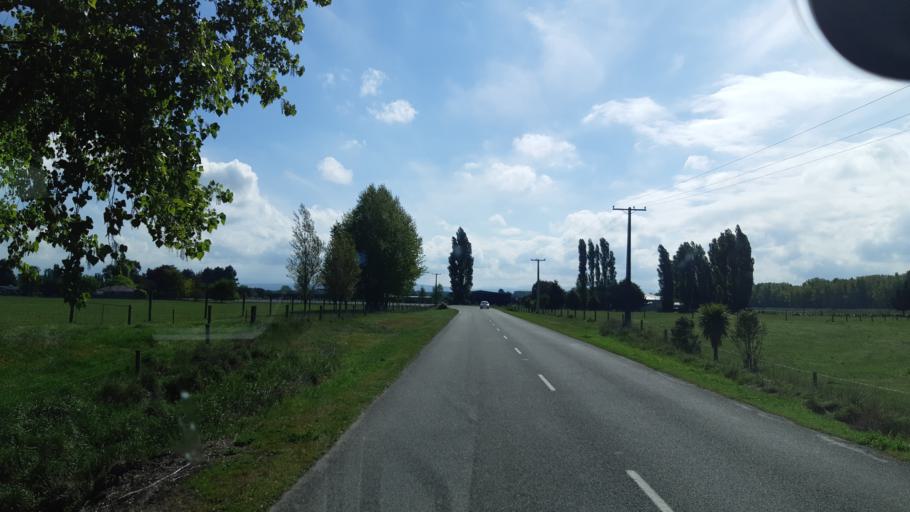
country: NZ
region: Canterbury
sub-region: Timaru District
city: Pleasant Point
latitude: -44.2523
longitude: 171.1372
